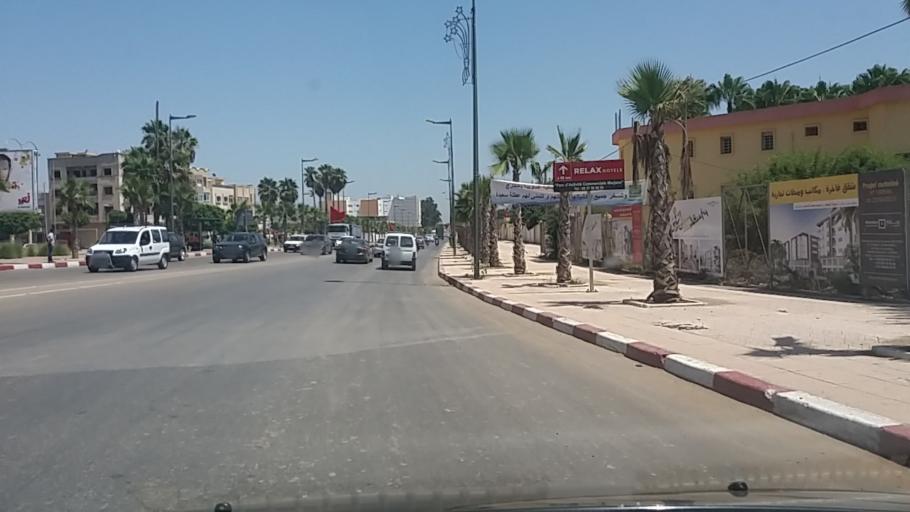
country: MA
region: Gharb-Chrarda-Beni Hssen
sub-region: Kenitra Province
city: Kenitra
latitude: 34.2485
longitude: -6.6147
